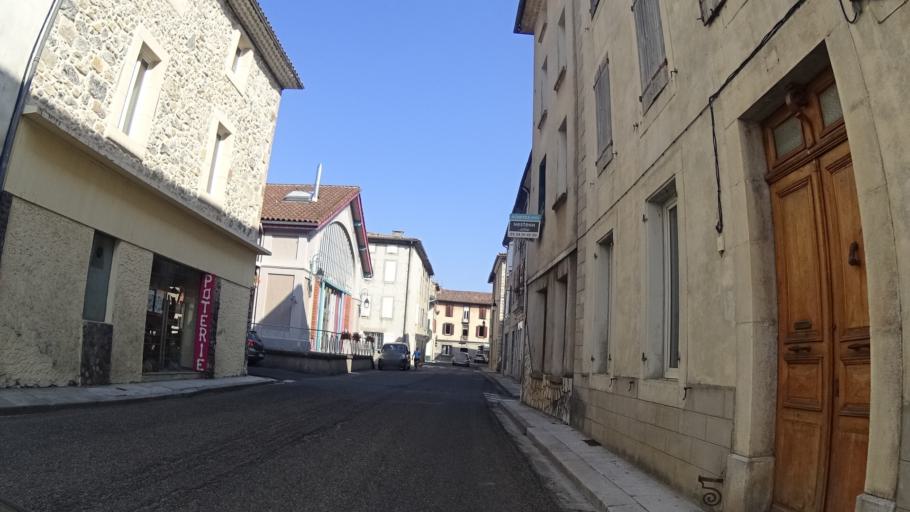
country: FR
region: Midi-Pyrenees
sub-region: Departement de l'Ariege
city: Belesta
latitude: 42.9027
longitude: 1.9350
